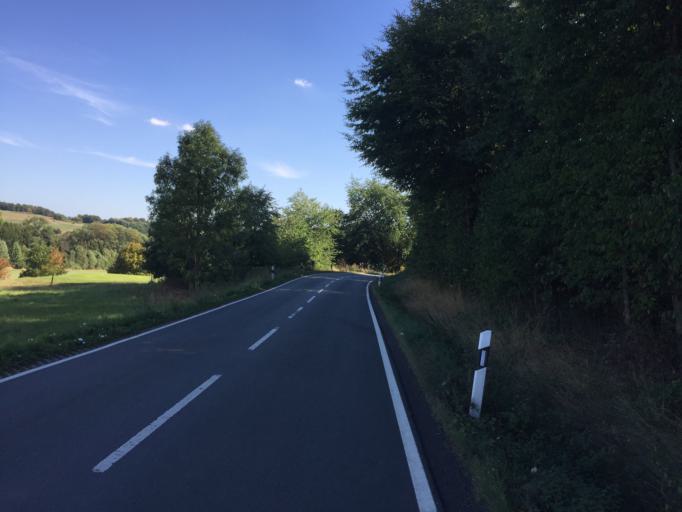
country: DE
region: Hesse
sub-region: Regierungsbezirk Giessen
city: Reiskirchen
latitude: 50.6099
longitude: 8.8572
